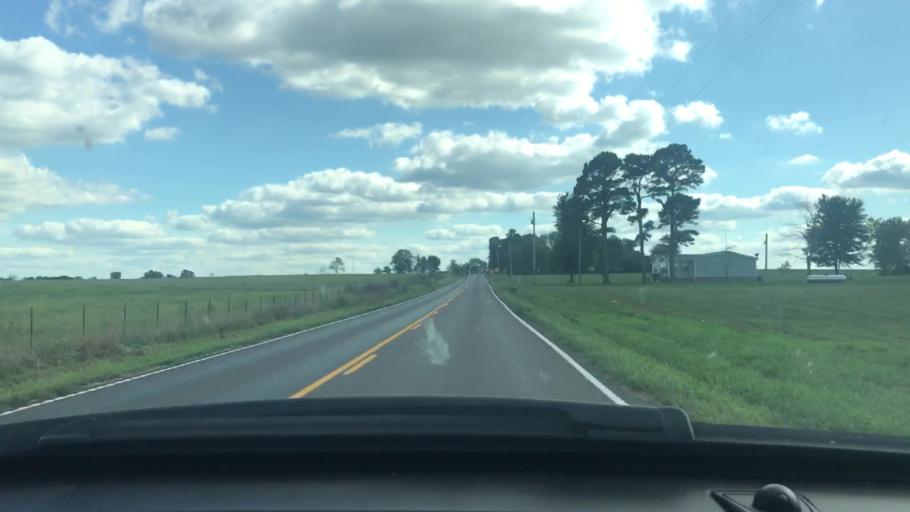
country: US
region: Missouri
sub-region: Wright County
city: Mountain Grove
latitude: 37.1702
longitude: -92.2672
